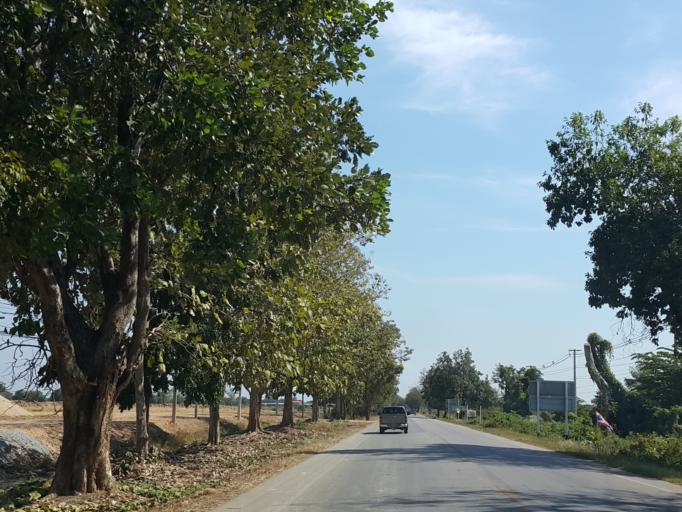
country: TH
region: Sukhothai
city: Sawankhalok
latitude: 17.3088
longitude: 99.7351
